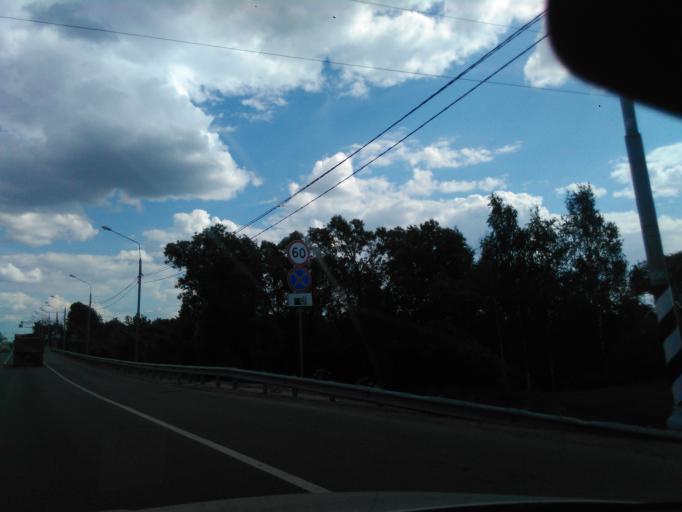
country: RU
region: Moskovskaya
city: Solnechnogorsk
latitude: 56.1664
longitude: 37.0110
